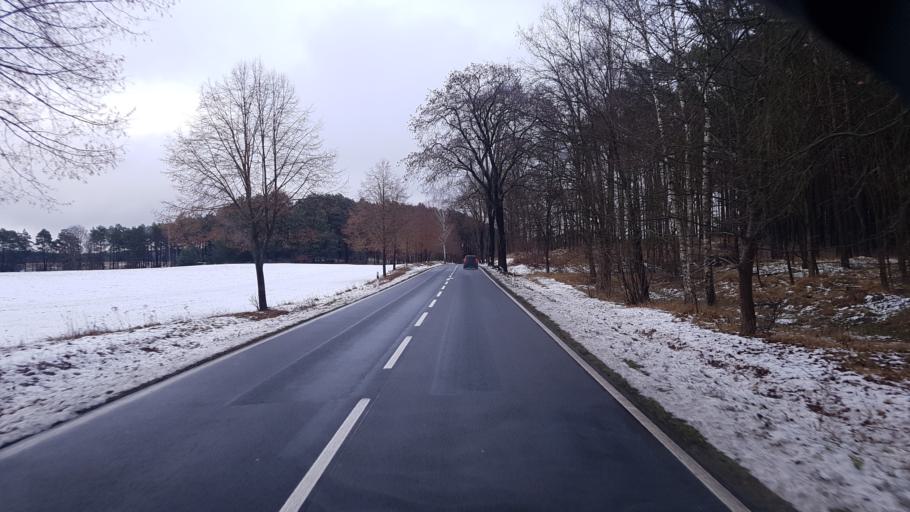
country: DE
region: Brandenburg
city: Jamlitz
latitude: 51.9872
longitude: 14.4003
